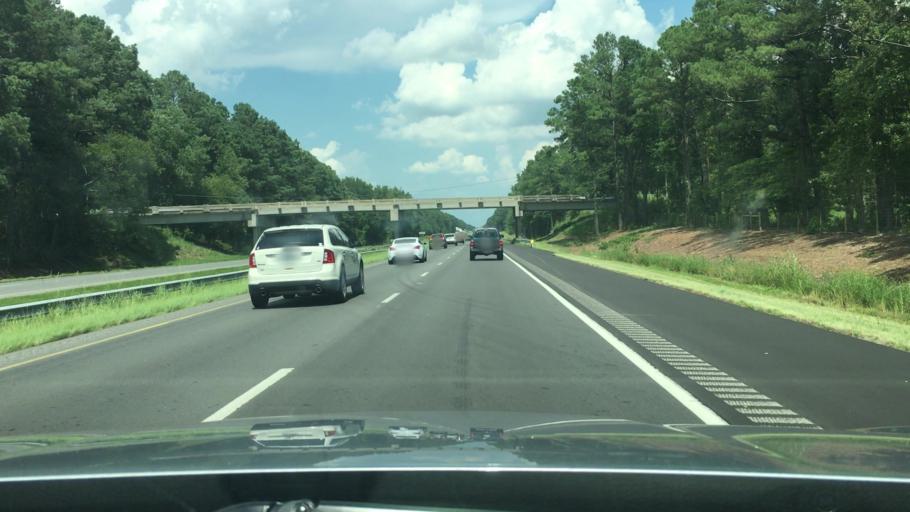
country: US
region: North Carolina
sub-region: Cumberland County
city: Eastover
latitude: 35.1406
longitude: -78.7356
